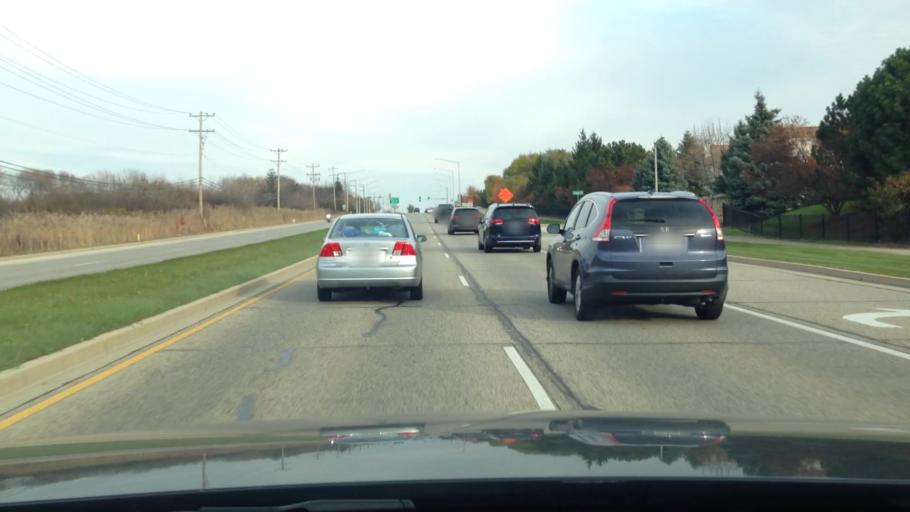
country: US
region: Illinois
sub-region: McHenry County
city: Lake in the Hills
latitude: 42.1757
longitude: -88.3469
